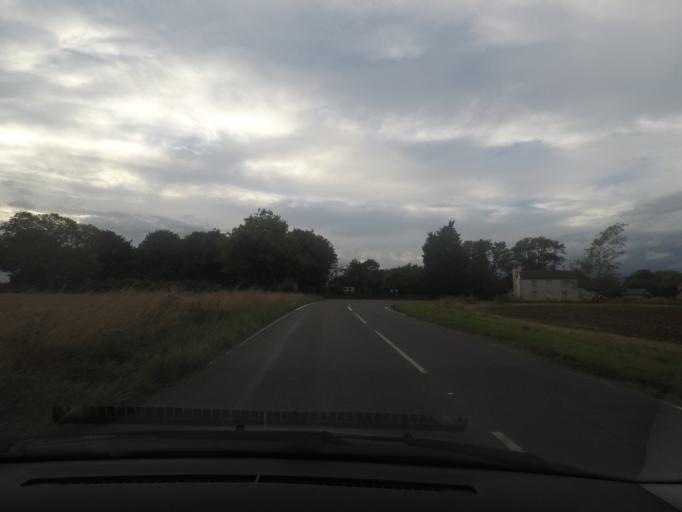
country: GB
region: England
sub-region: Lincolnshire
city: Alford
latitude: 53.2270
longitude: 0.1275
